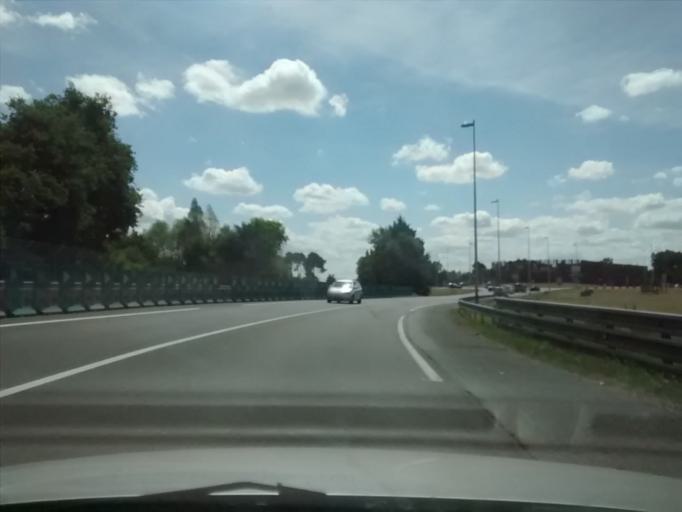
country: FR
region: Pays de la Loire
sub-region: Departement de la Sarthe
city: Ruaudin
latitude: 47.9569
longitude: 0.2275
